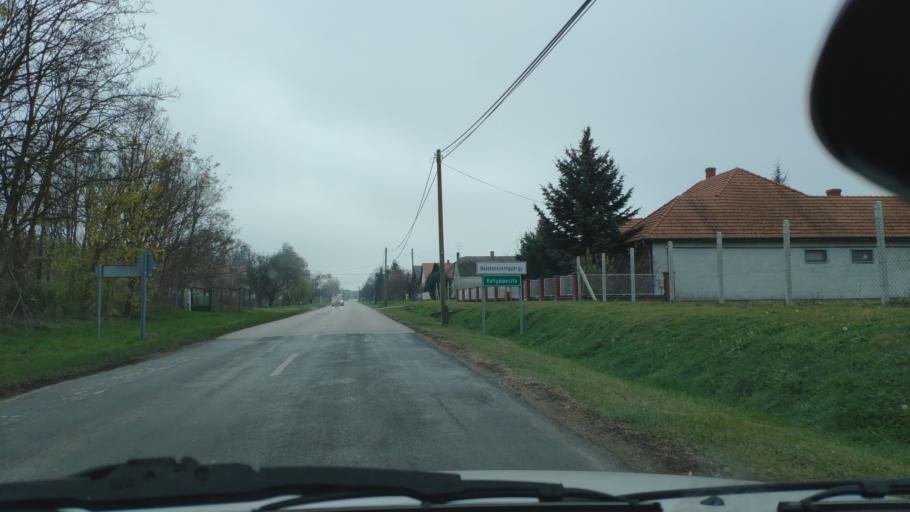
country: HU
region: Somogy
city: Balatonbereny
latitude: 46.6769
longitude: 17.2873
